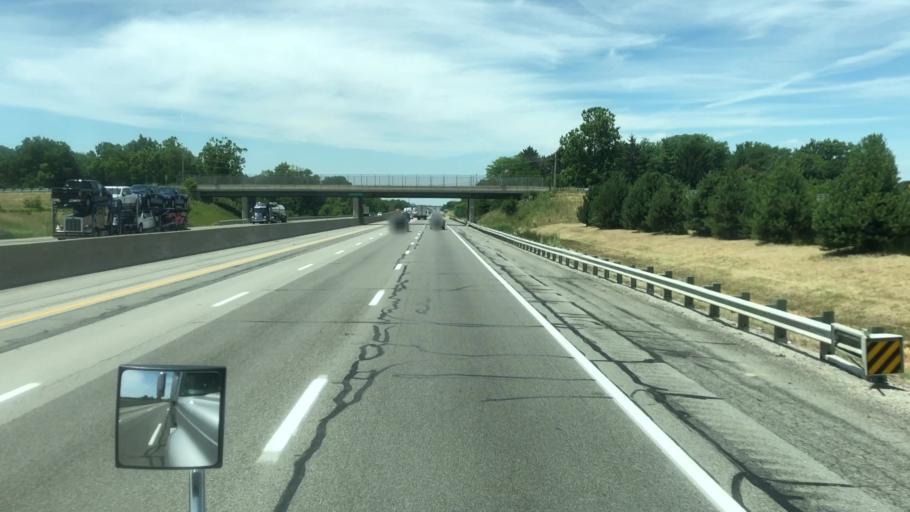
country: US
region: Ohio
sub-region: Ottawa County
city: Elmore
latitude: 41.4666
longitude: -83.3042
